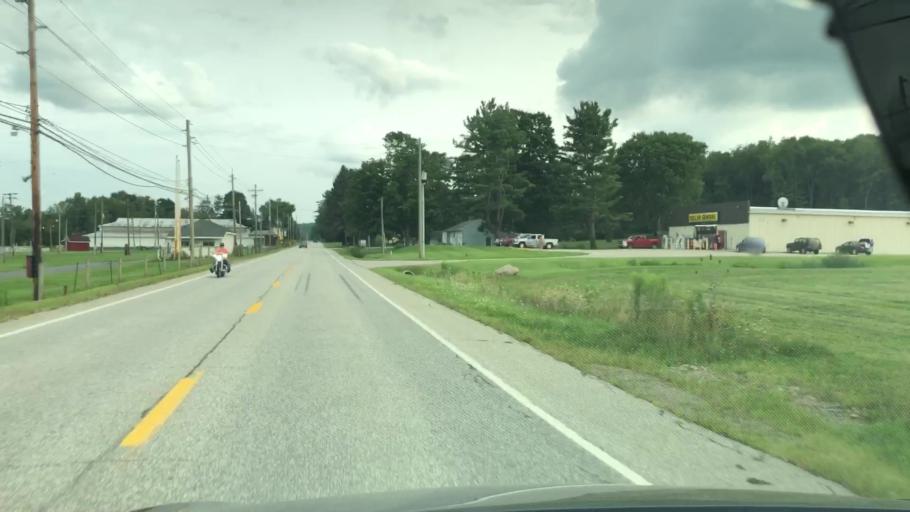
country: US
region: Pennsylvania
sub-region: Erie County
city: Union City
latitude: 42.0144
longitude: -79.8159
